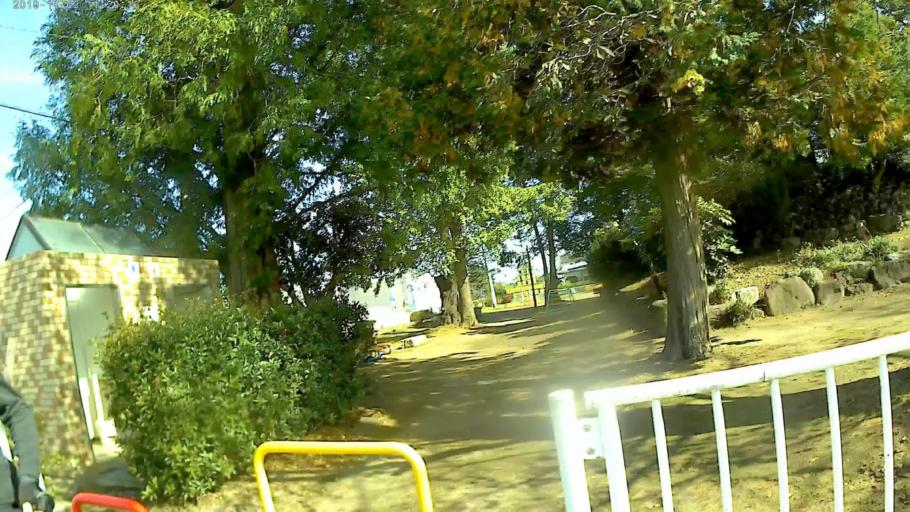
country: JP
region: Gunma
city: Annaka
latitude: 36.3131
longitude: 138.8551
